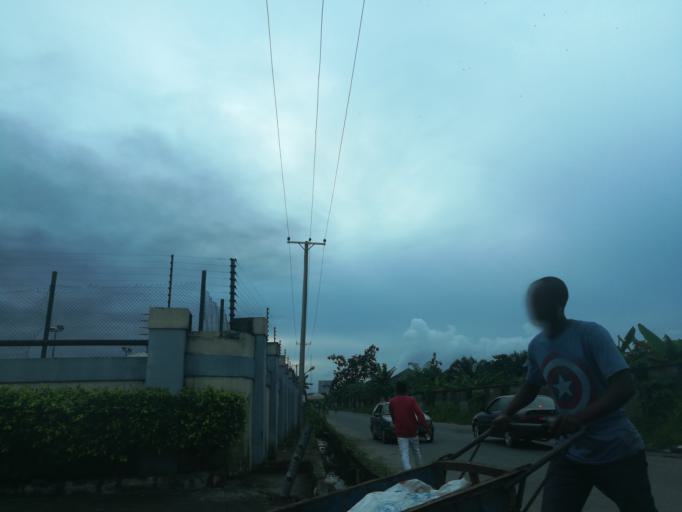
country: NG
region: Rivers
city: Port Harcourt
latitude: 4.8192
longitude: 6.9869
